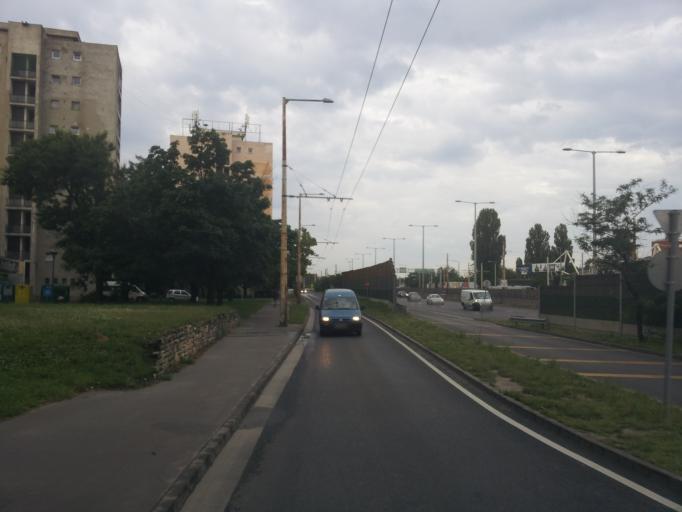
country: HU
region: Budapest
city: Budapest XIV. keruelet
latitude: 47.5228
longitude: 19.0942
